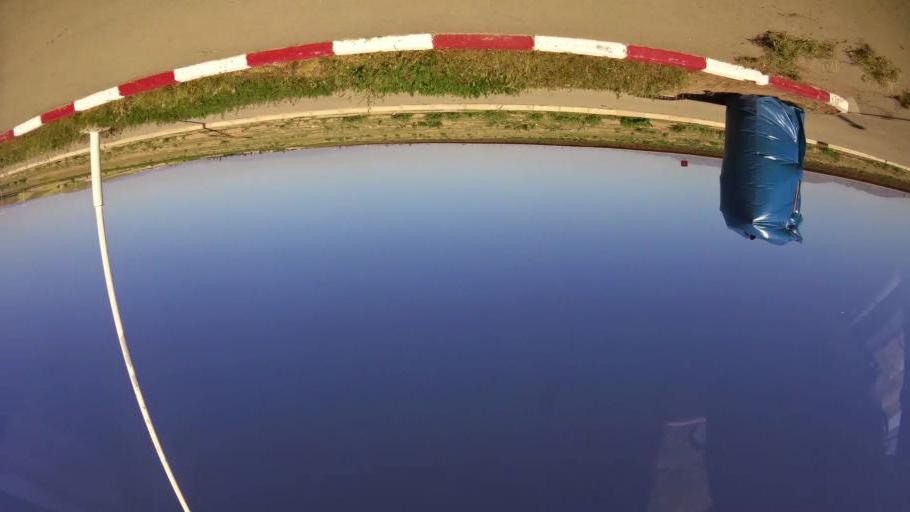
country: MA
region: Oriental
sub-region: Oujda-Angad
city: Oujda
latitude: 34.7740
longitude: -1.9308
